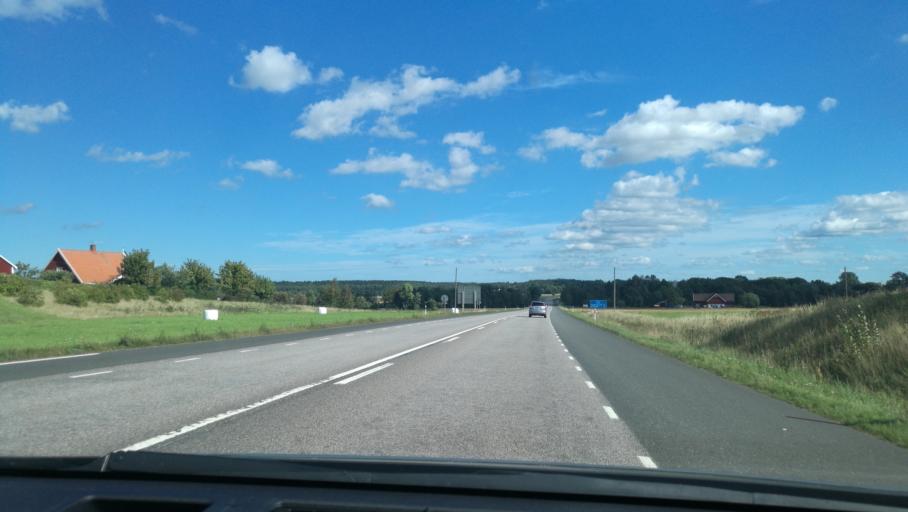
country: SE
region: Vaestra Goetaland
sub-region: Gotene Kommun
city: Kallby
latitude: 58.5060
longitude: 13.3155
